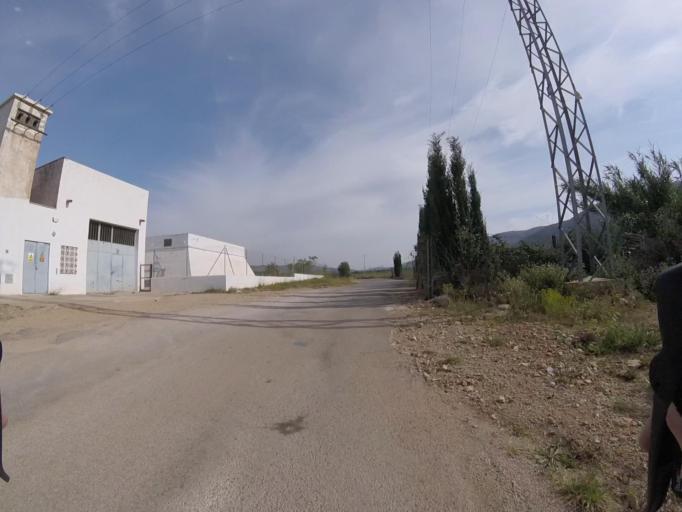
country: ES
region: Valencia
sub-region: Provincia de Castello
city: Alcoceber
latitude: 40.2600
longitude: 0.2528
